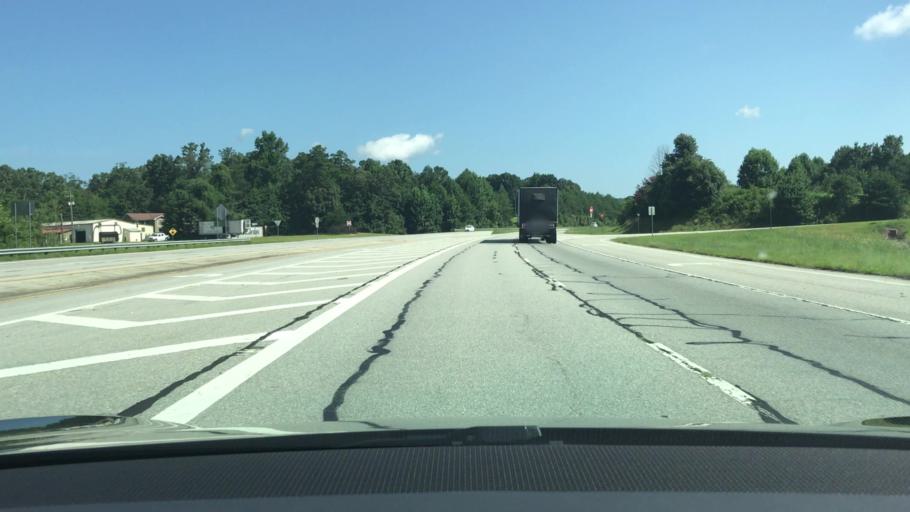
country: US
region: Georgia
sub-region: Habersham County
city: Clarkesville
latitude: 34.6877
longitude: -83.4244
